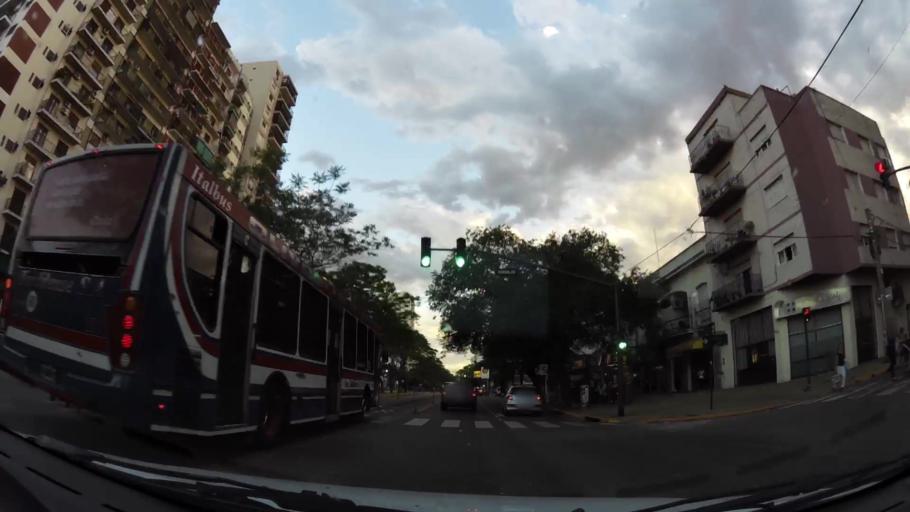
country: AR
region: Buenos Aires
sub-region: Partido de Vicente Lopez
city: Olivos
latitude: -34.5230
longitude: -58.4844
